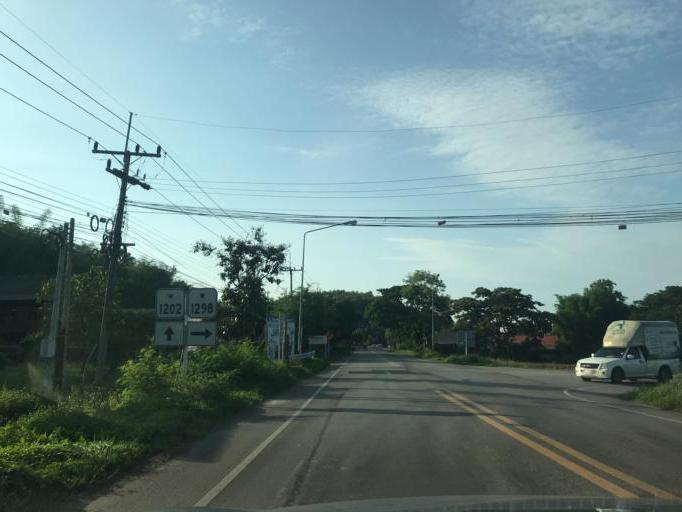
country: TH
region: Phayao
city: Phu Kam Yao
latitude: 19.3119
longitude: 100.0037
